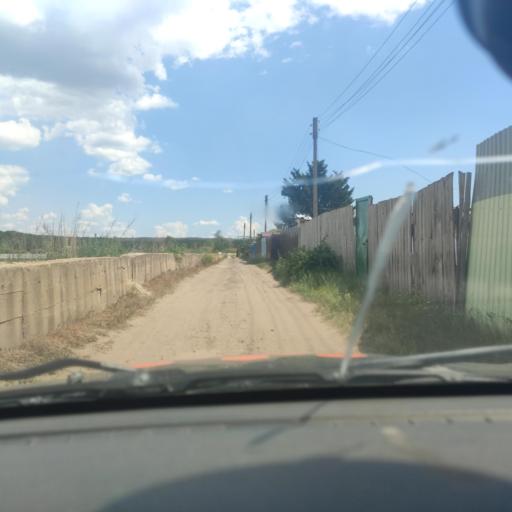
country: RU
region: Samara
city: Zhigulevsk
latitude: 53.5006
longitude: 49.4954
